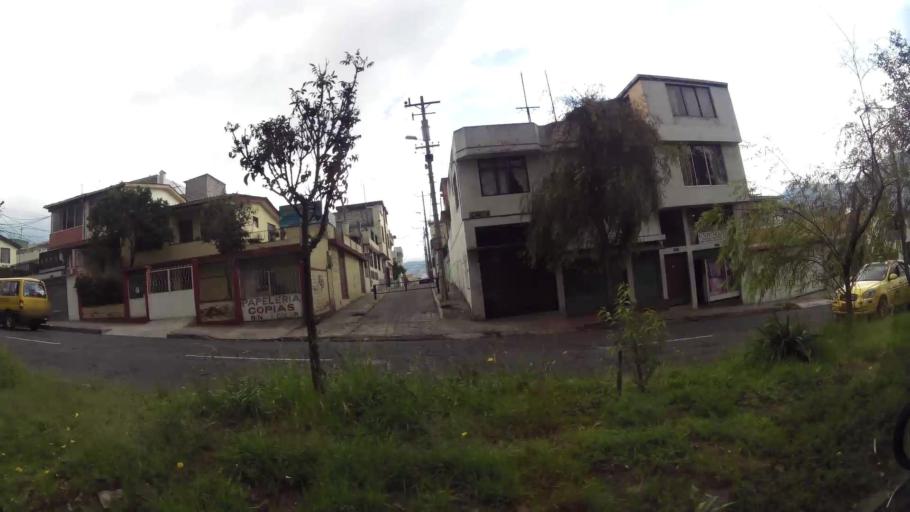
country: EC
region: Pichincha
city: Quito
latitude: -0.0896
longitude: -78.4674
